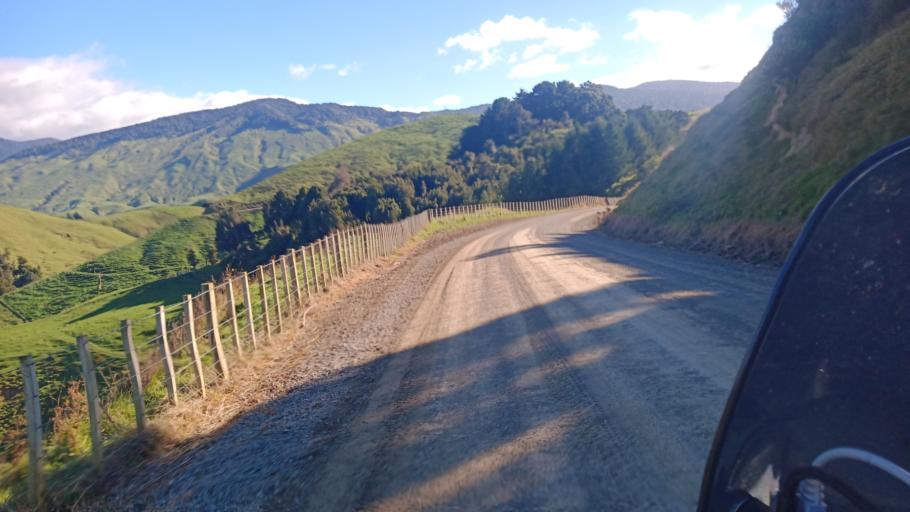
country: NZ
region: Hawke's Bay
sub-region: Wairoa District
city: Wairoa
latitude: -38.7842
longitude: 177.2689
